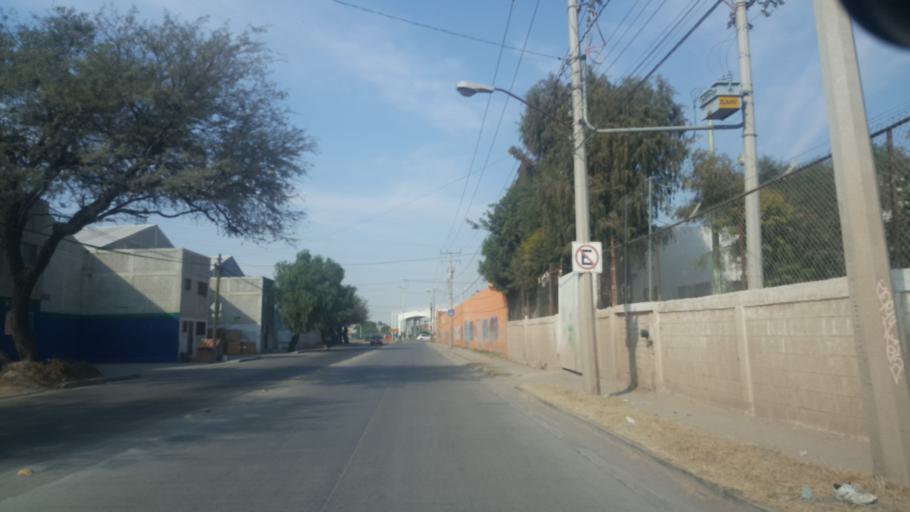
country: MX
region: Guanajuato
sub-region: Leon
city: Fraccionamiento Paraiso Real
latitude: 21.1046
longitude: -101.6216
